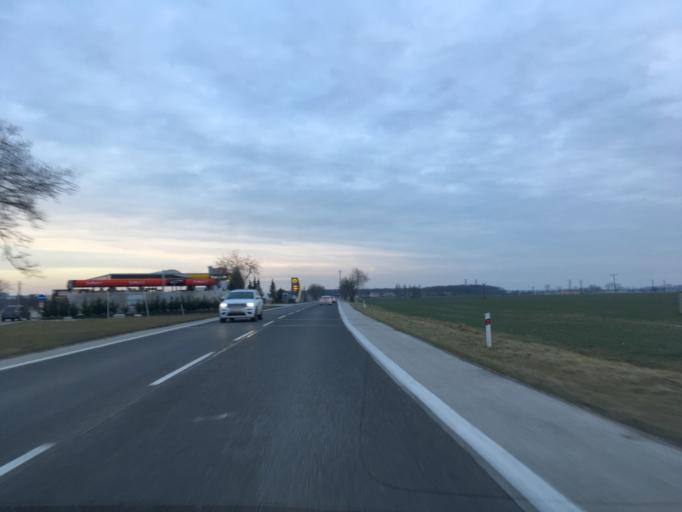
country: SK
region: Trnavsky
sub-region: Okres Dunajska Streda
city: Velky Meder
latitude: 47.8702
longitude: 17.7576
